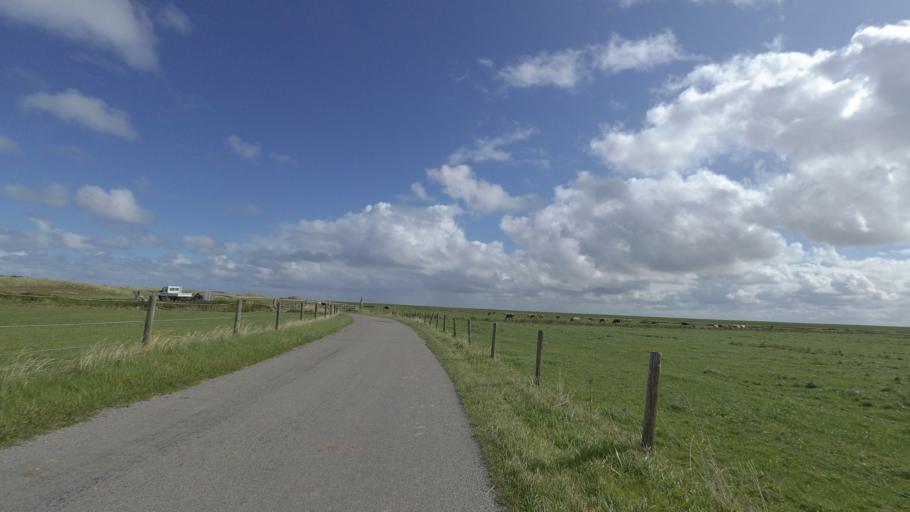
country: NL
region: Friesland
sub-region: Gemeente Ameland
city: Nes
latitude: 53.4483
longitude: 5.8408
